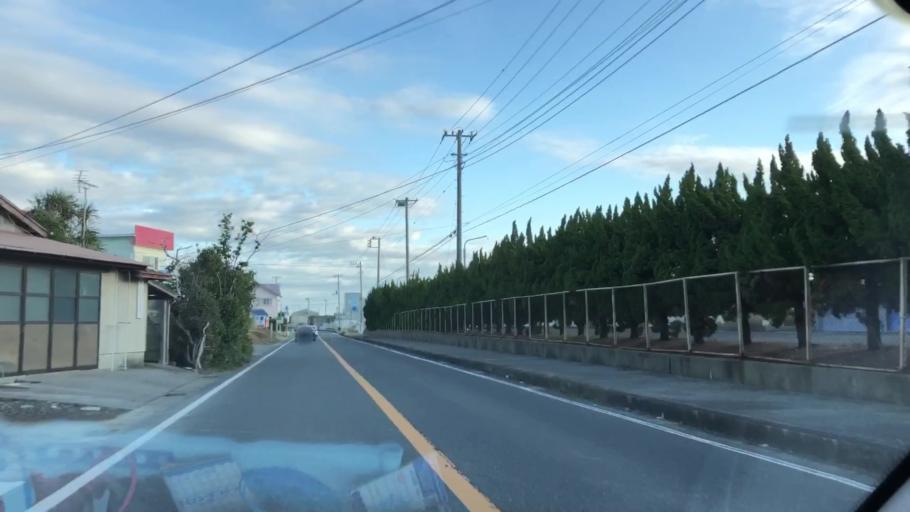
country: JP
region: Chiba
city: Tateyama
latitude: 34.9382
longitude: 139.9589
